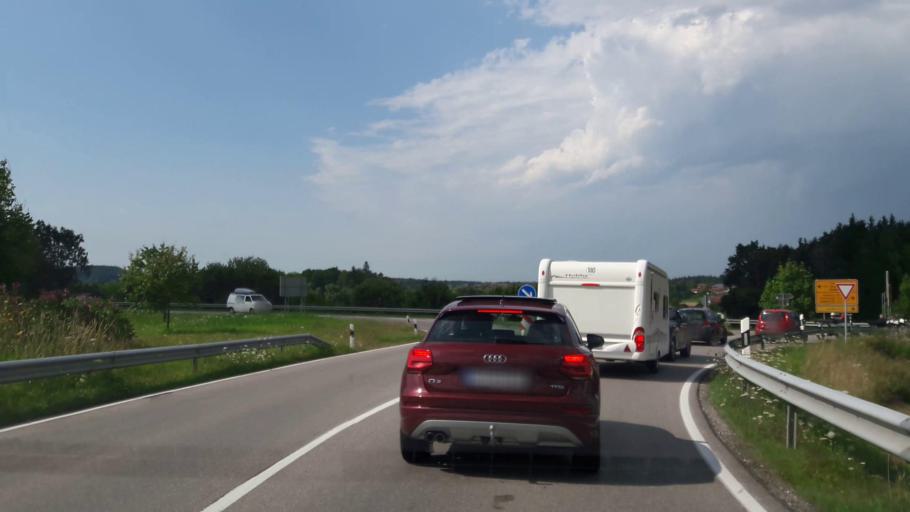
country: DE
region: Bavaria
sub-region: Upper Bavaria
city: Teisendorf
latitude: 47.8376
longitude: 12.8316
